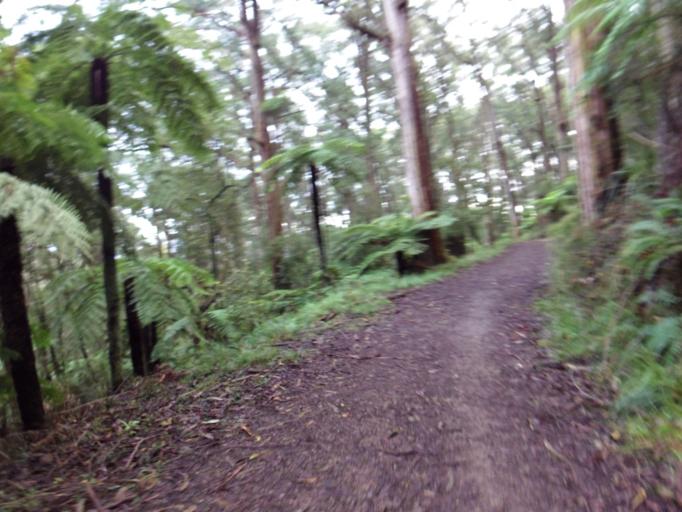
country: AU
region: Victoria
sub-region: Yarra Ranges
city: Olinda
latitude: -37.8486
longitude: 145.3519
